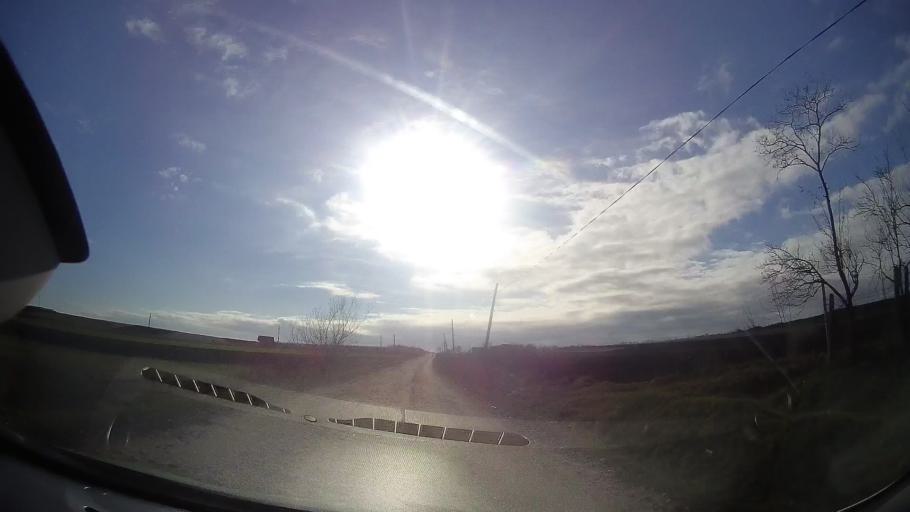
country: RO
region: Mures
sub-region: Comuna Papiu Ilarian
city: Papiu Ilarian
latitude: 46.5681
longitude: 24.2092
